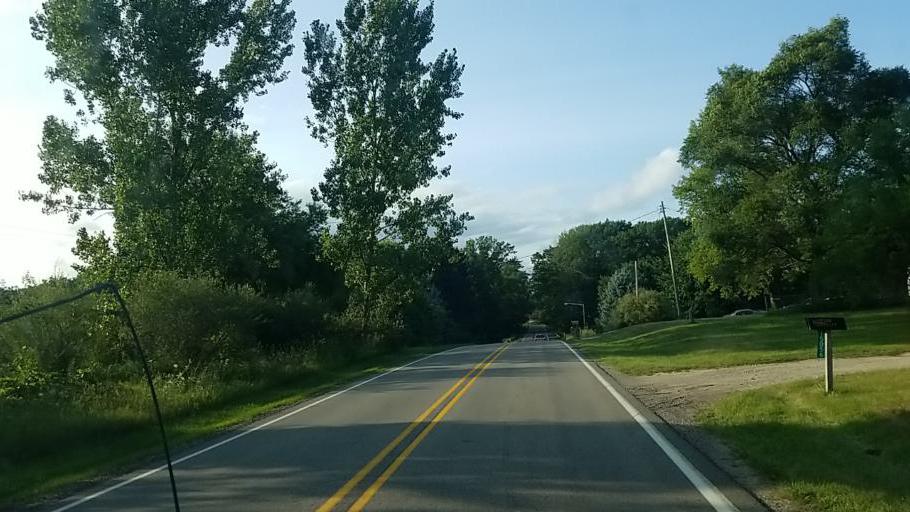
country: US
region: Michigan
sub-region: Montcalm County
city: Greenville
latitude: 43.2400
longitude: -85.3693
